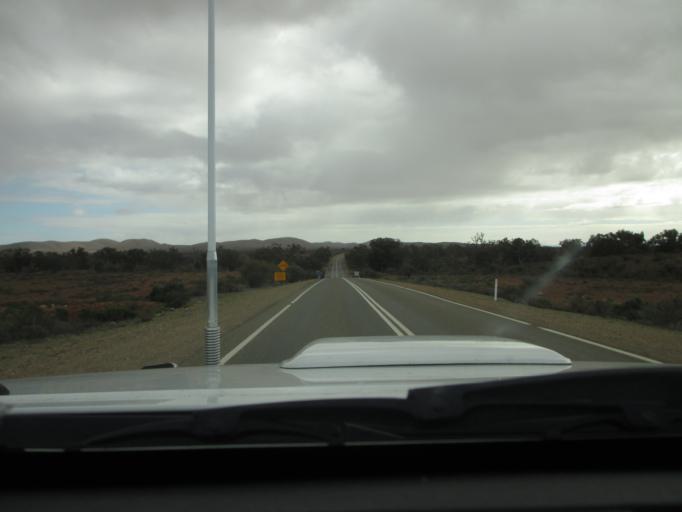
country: AU
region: South Australia
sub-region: Flinders Ranges
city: Quorn
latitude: -31.5520
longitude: 138.4264
